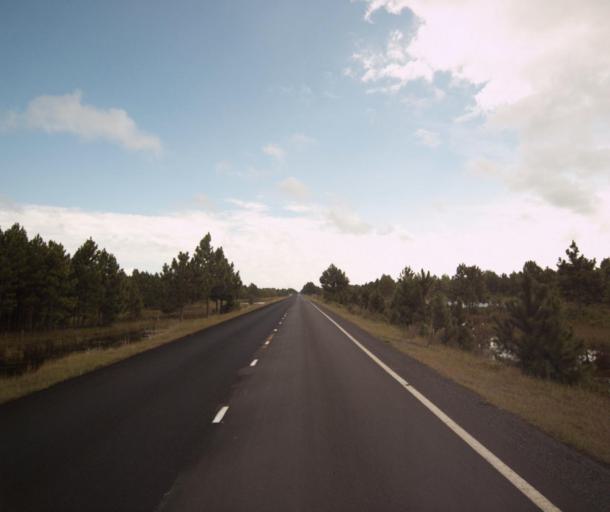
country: BR
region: Rio Grande do Sul
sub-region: Tapes
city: Tapes
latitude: -31.4230
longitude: -51.1813
